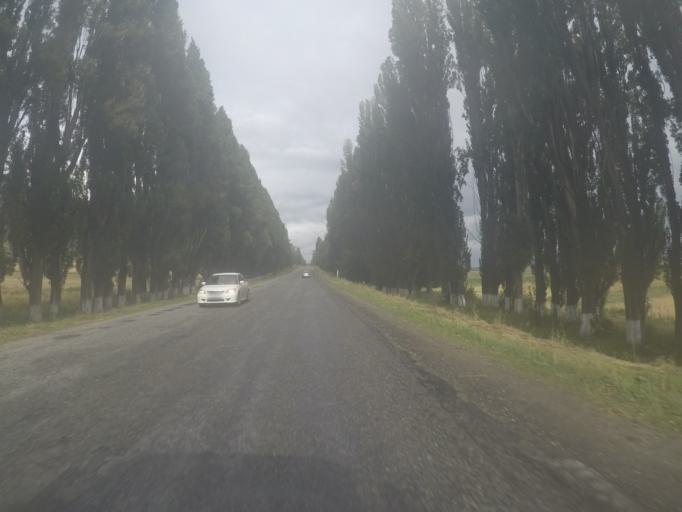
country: KG
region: Ysyk-Koel
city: Tyup
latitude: 42.7427
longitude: 78.0363
